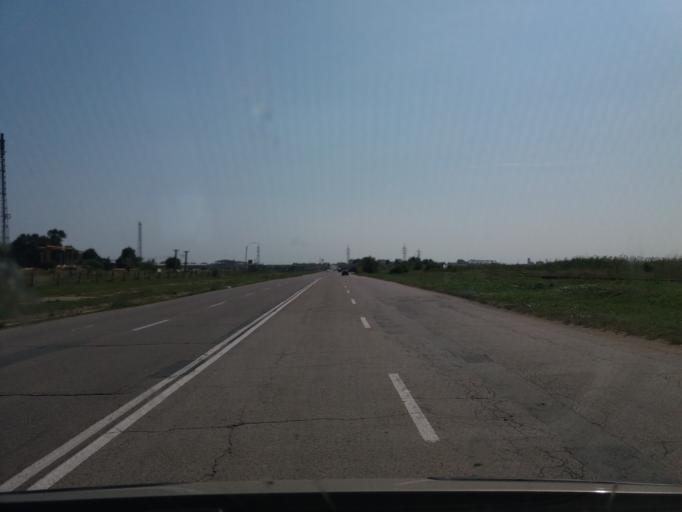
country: RO
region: Constanta
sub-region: Comuna Navodari
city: Navodari
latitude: 44.3340
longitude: 28.6325
